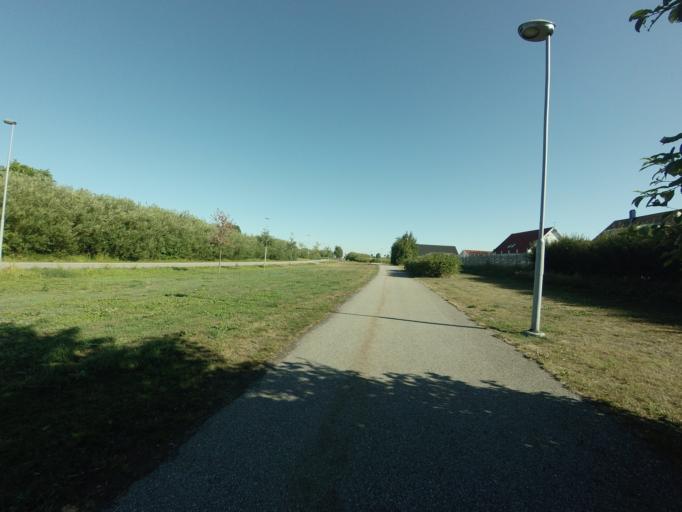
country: SE
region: Skane
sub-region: Trelleborgs Kommun
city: Skare
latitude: 55.4072
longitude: 13.0714
